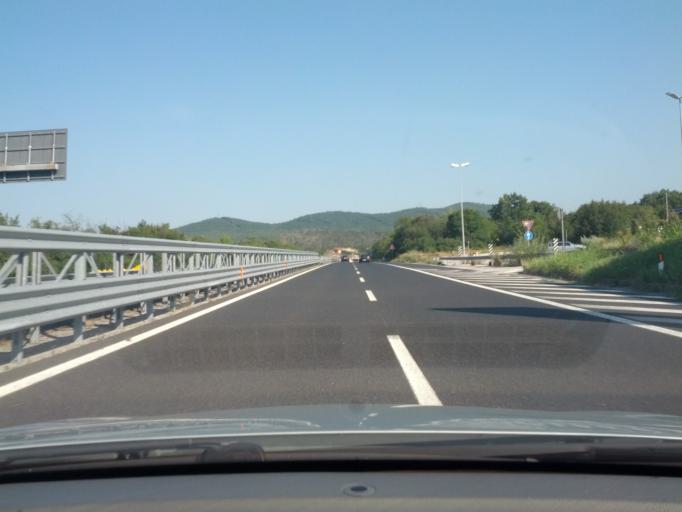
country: IT
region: Friuli Venezia Giulia
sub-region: Provincia di Trieste
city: Sistiana-Visogliano
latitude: 45.7690
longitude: 13.6463
